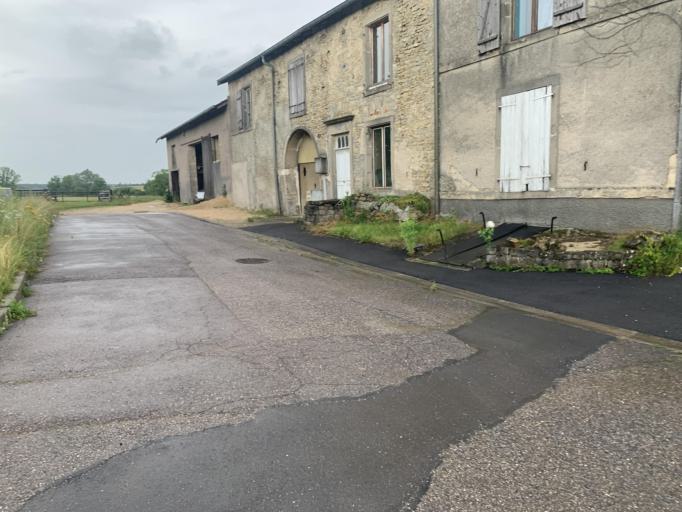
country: FR
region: Lorraine
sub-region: Departement des Vosges
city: Chatenois
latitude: 48.2863
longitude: 5.8487
